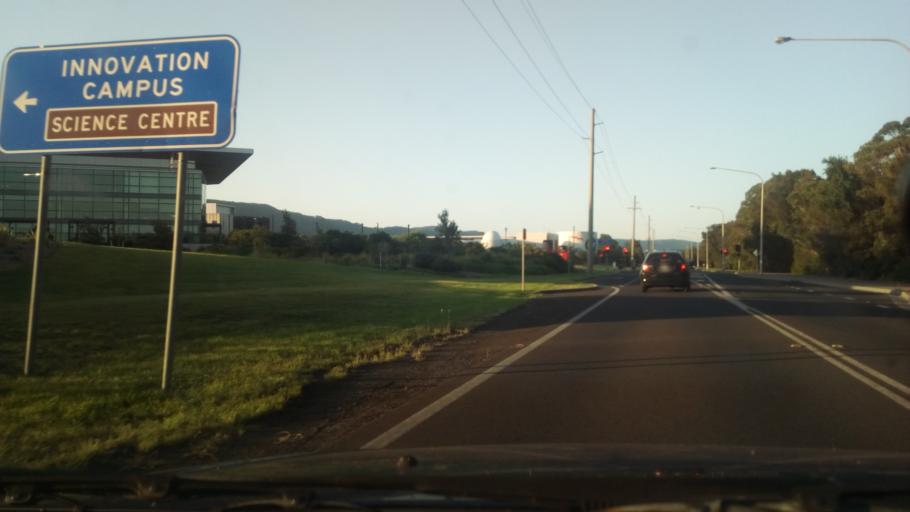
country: AU
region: New South Wales
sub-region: Wollongong
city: Fairy Meadow
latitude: -34.4034
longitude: 150.9001
